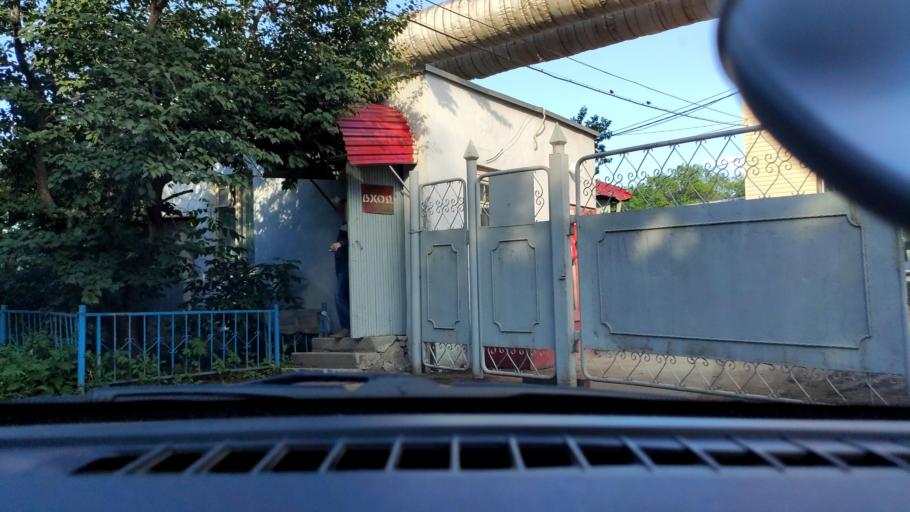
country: RU
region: Samara
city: Samara
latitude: 53.1990
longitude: 50.2277
